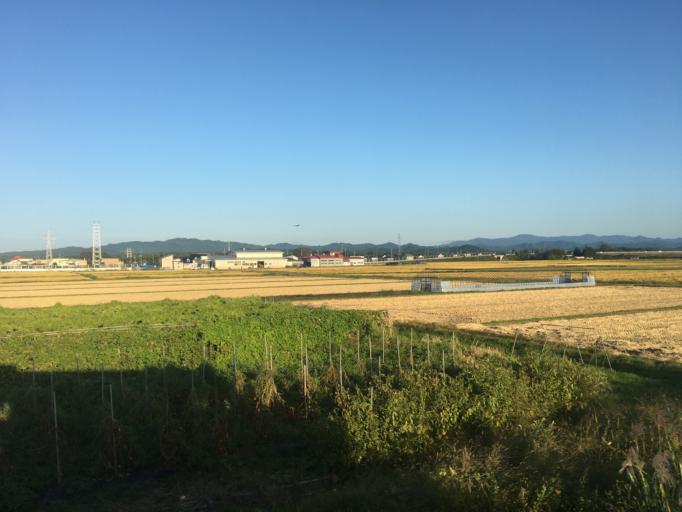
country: JP
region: Akita
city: Takanosu
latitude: 40.2209
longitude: 140.3561
